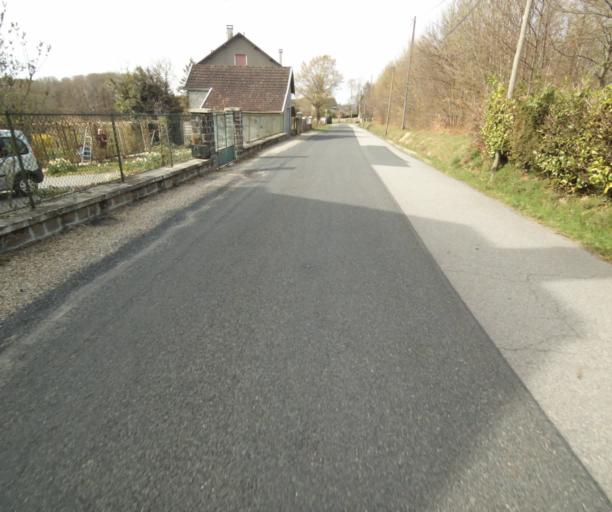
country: FR
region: Limousin
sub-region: Departement de la Correze
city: Correze
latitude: 45.4218
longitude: 1.8324
